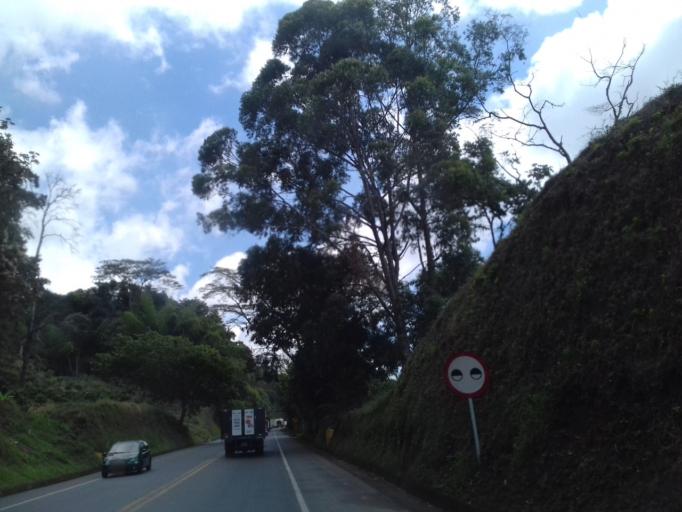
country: CO
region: Risaralda
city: Pereira
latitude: 4.8230
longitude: -75.7215
